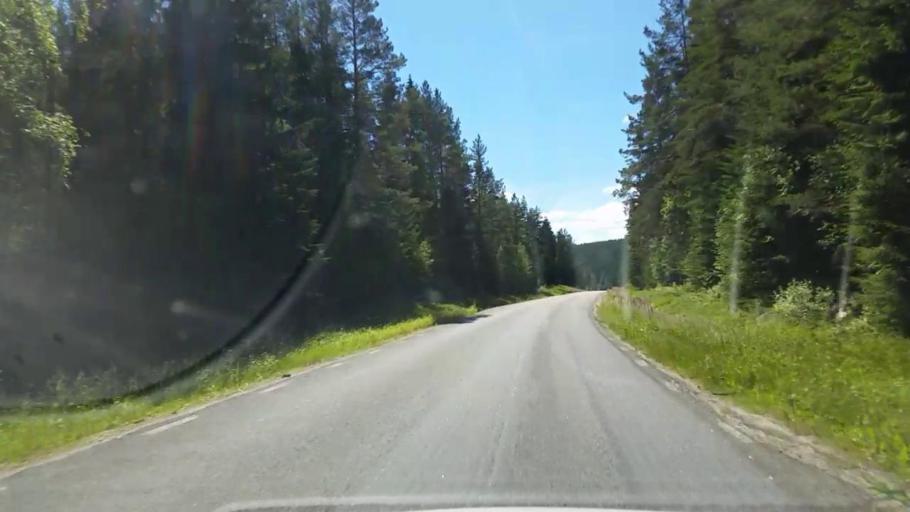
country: SE
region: Gaevleborg
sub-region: Ljusdals Kommun
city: Farila
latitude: 61.6681
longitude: 15.6125
